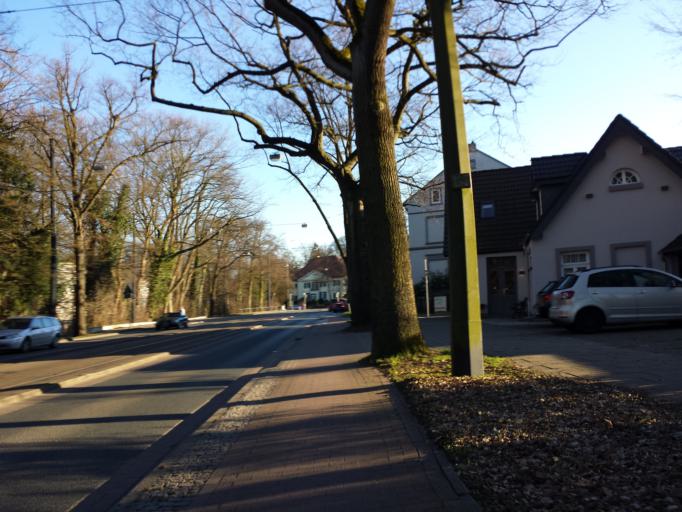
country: DE
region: Lower Saxony
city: Lilienthal
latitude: 53.0927
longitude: 8.8709
